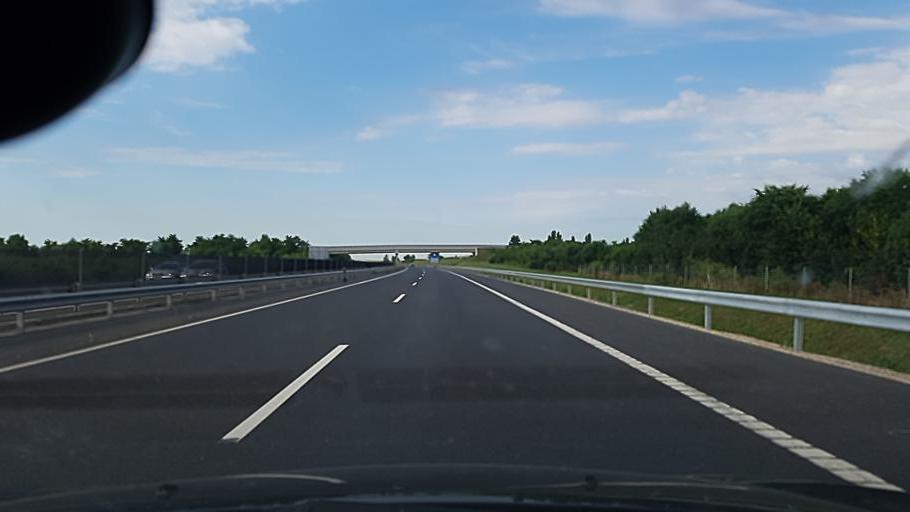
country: HU
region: Pest
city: Szazhalombatta
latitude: 47.3162
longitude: 18.8705
